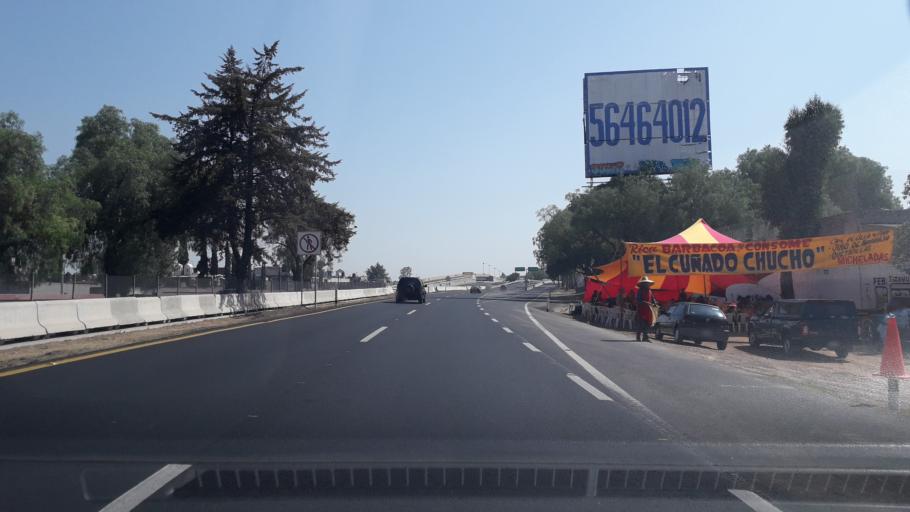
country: MX
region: Mexico
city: Santo Tomas Chiconautla
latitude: 19.6584
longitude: -99.0084
